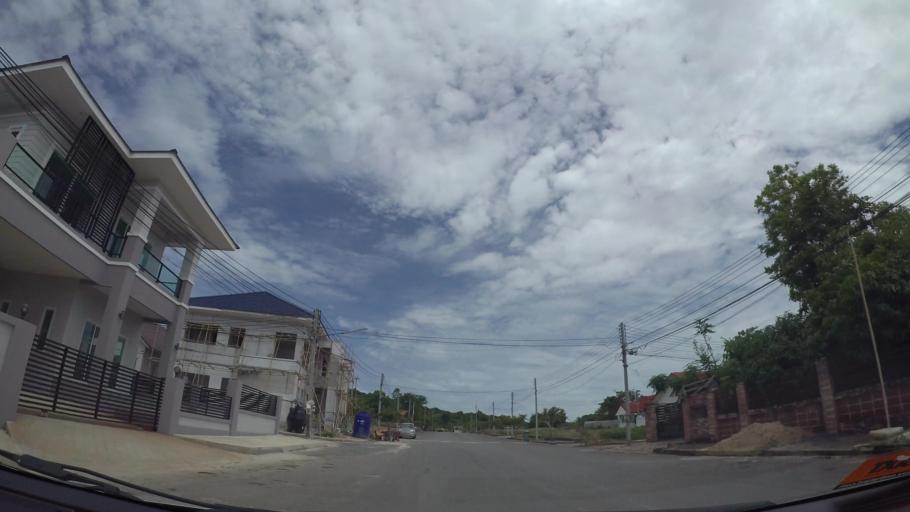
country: TH
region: Chon Buri
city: Sattahip
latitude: 12.6895
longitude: 100.8862
